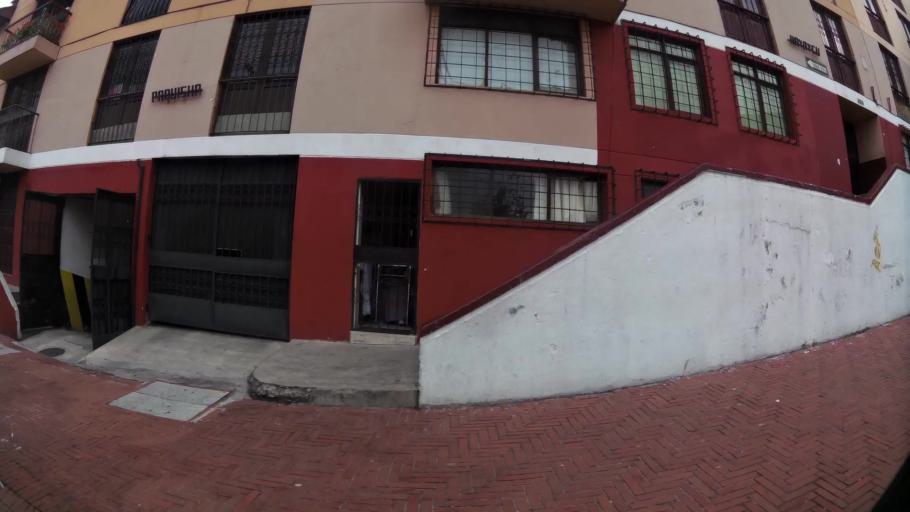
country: EC
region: Pichincha
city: Quito
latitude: -0.2157
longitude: -78.5101
